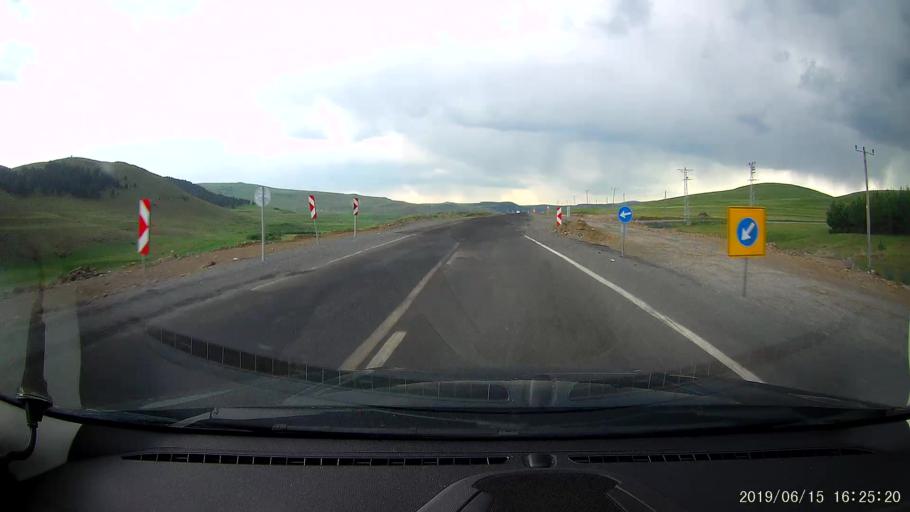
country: TR
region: Ardahan
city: Hanak
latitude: 41.1550
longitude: 42.8706
